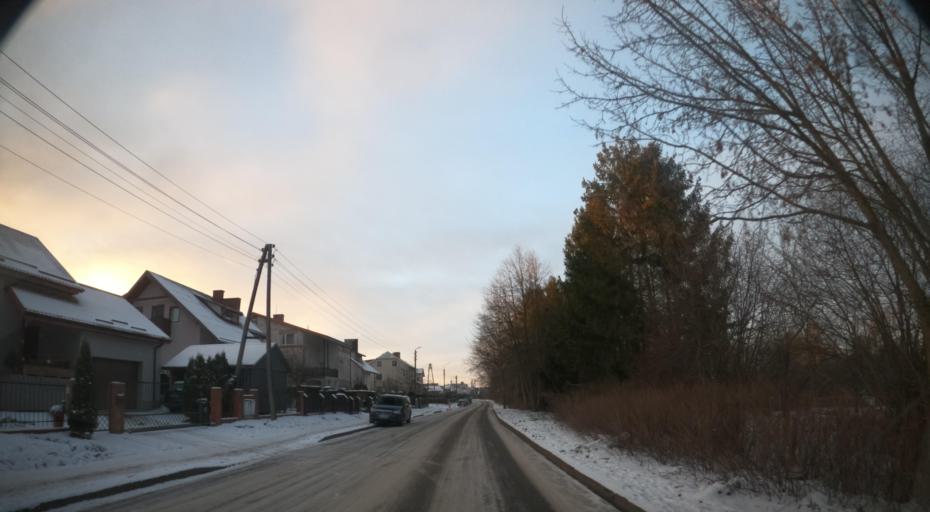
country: PL
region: West Pomeranian Voivodeship
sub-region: Powiat koszalinski
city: Sianow
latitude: 54.2345
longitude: 16.3056
